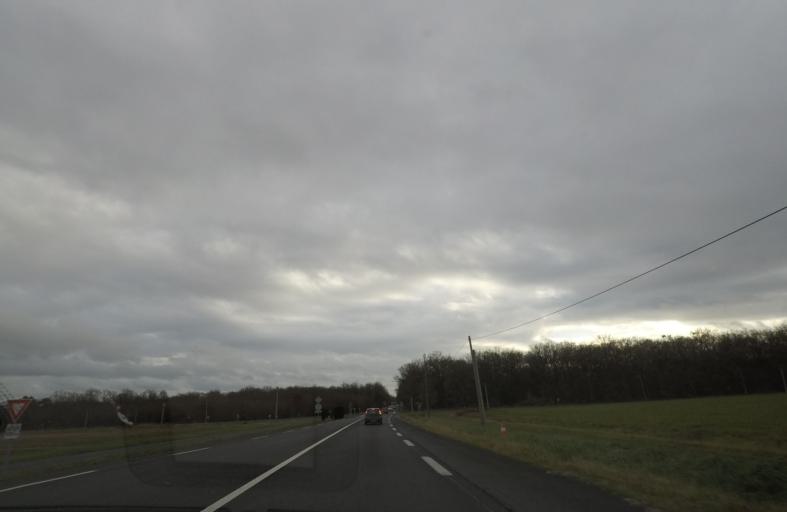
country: FR
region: Centre
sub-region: Departement du Loir-et-Cher
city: Soings-en-Sologne
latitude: 47.4397
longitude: 1.5498
